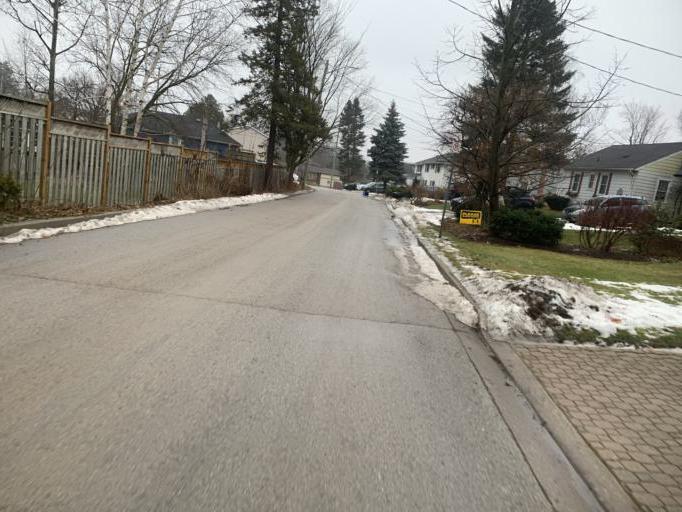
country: CA
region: Ontario
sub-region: Halton
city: Milton
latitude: 43.6581
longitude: -79.9268
